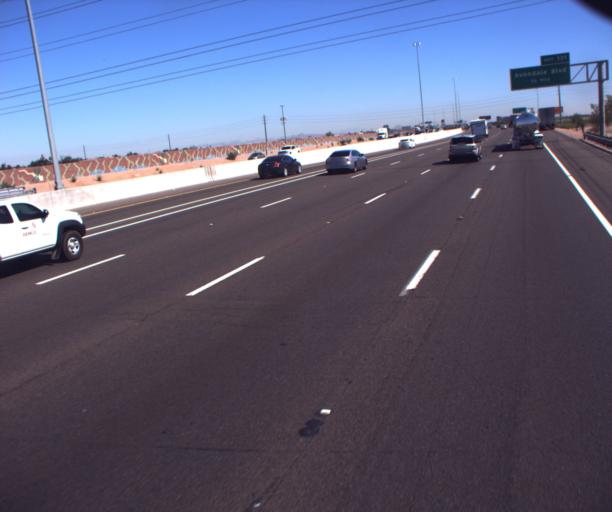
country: US
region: Arizona
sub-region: Maricopa County
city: Avondale
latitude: 33.4575
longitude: -112.3198
